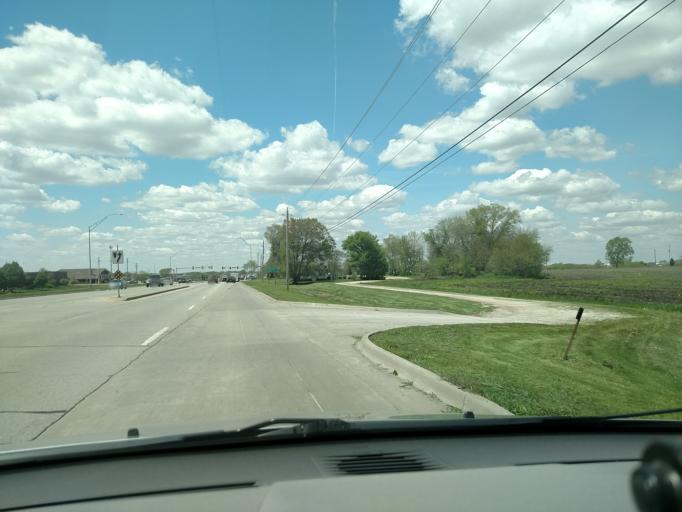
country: US
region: Iowa
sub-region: Polk County
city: Ankeny
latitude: 41.7029
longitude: -93.5974
